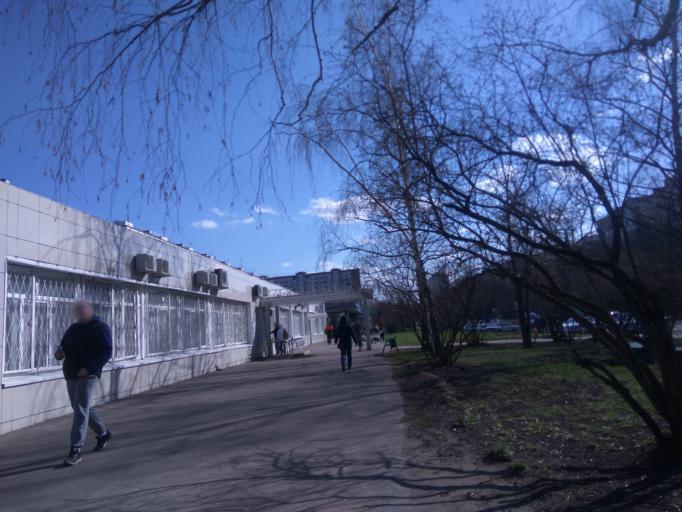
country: RU
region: Moscow
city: Ivanovskoye
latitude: 55.7646
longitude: 37.8330
